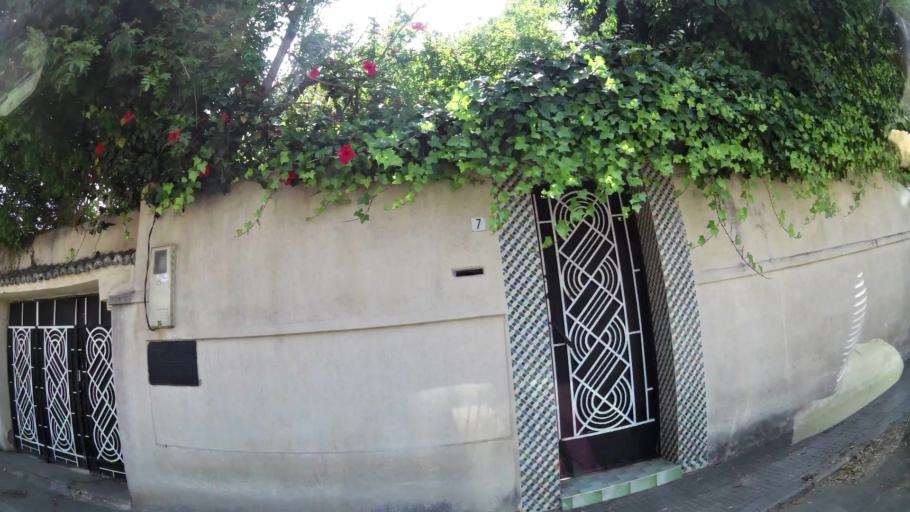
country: MA
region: Rabat-Sale-Zemmour-Zaer
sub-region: Rabat
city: Rabat
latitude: 34.0145
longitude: -6.8412
